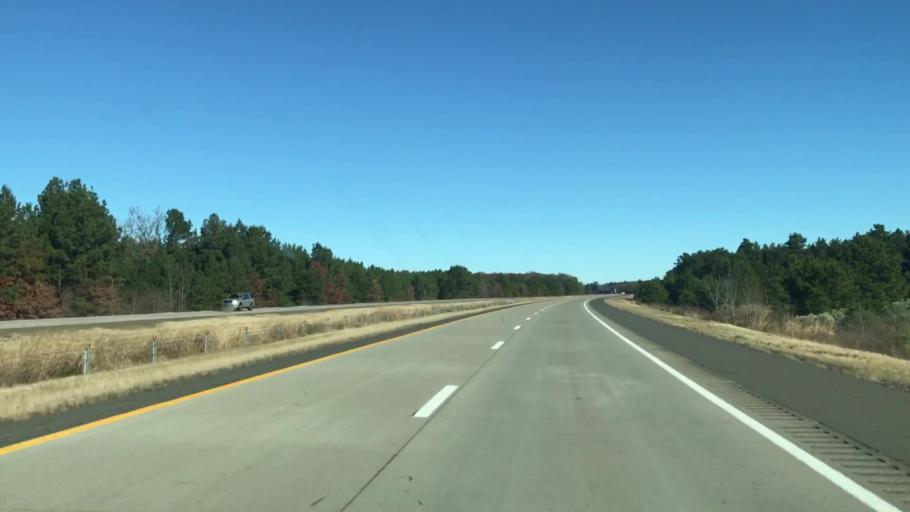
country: US
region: Texas
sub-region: Cass County
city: Queen City
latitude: 33.2016
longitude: -93.8769
